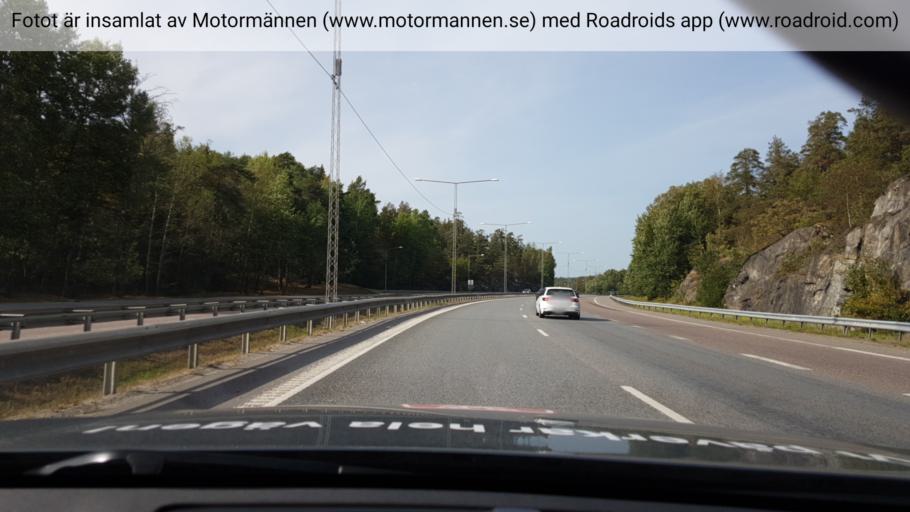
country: SE
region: Stockholm
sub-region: Nacka Kommun
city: Alta
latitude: 59.2515
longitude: 18.1703
